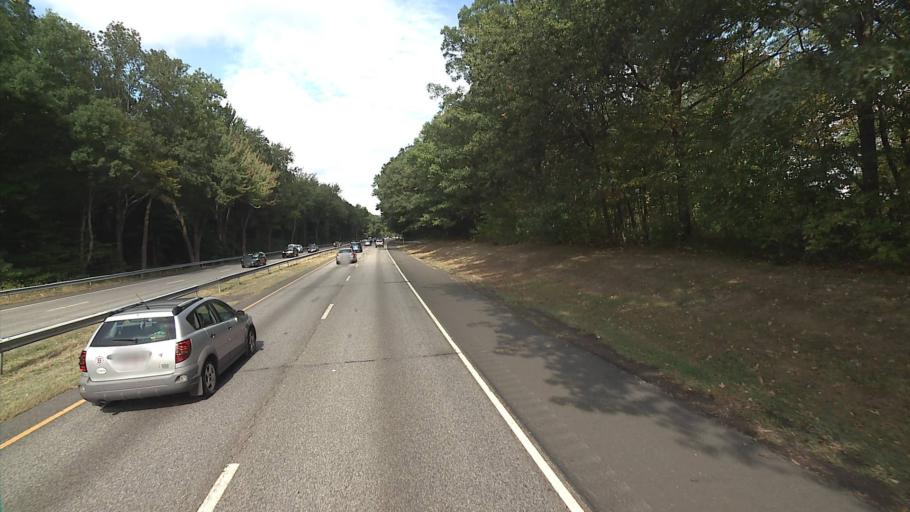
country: US
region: Connecticut
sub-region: New Haven County
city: Wallingford
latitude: 41.4785
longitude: -72.8234
